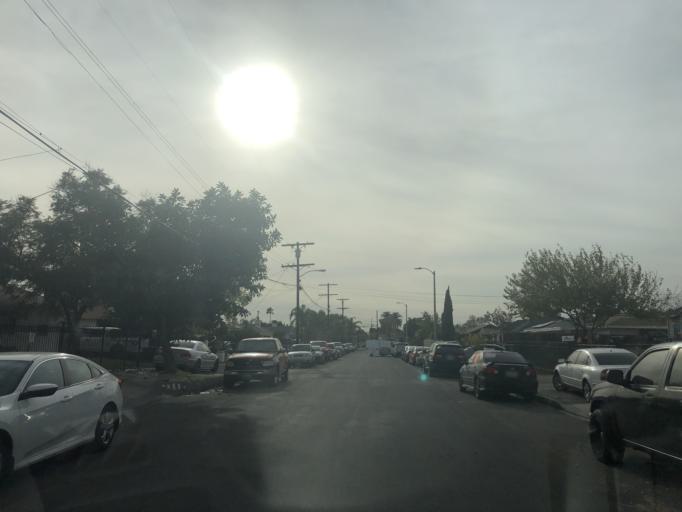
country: US
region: California
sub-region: Los Angeles County
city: San Fernando
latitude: 34.2702
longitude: -118.4273
